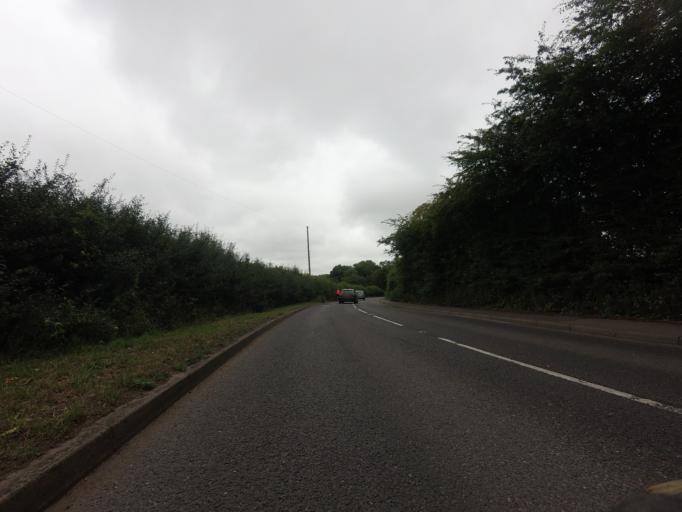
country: GB
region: England
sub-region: Kent
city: Dartford
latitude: 51.4181
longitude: 0.2390
